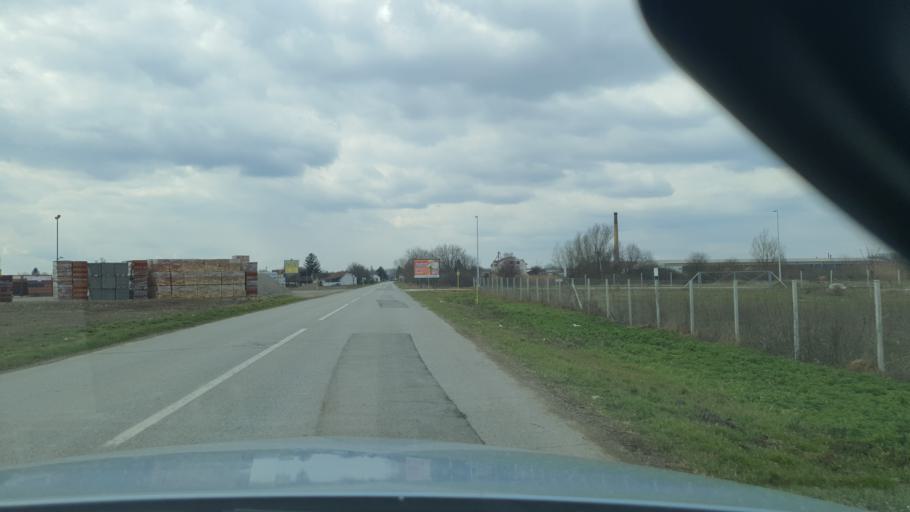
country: RS
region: Autonomna Pokrajina Vojvodina
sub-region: Juznobacki Okrug
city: Bac
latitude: 45.3965
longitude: 19.2501
